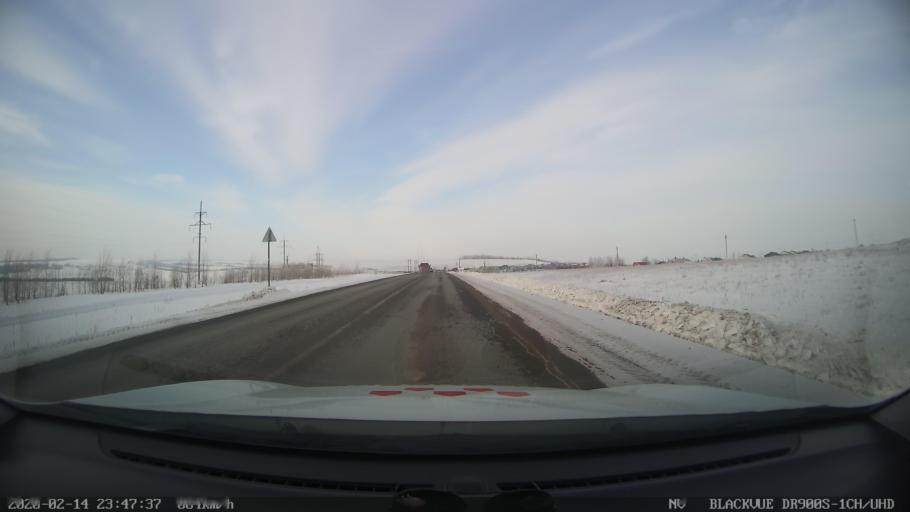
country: RU
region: Tatarstan
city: Kuybyshevskiy Zaton
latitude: 55.2408
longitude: 49.2077
